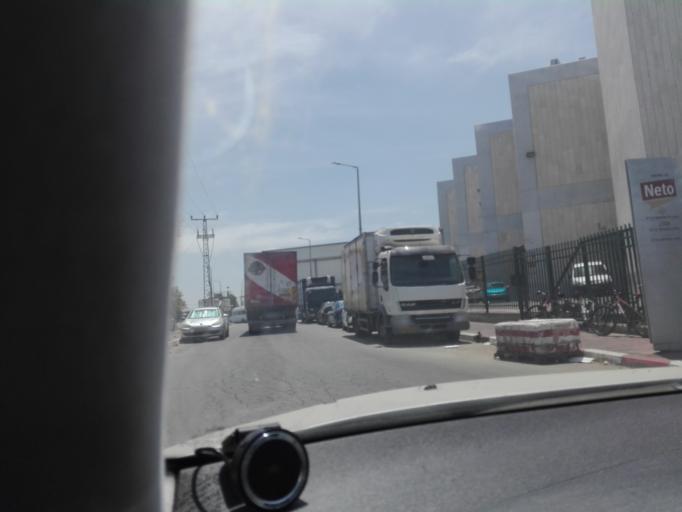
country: IL
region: Central District
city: Bene 'Ayish
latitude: 31.7396
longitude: 34.7492
